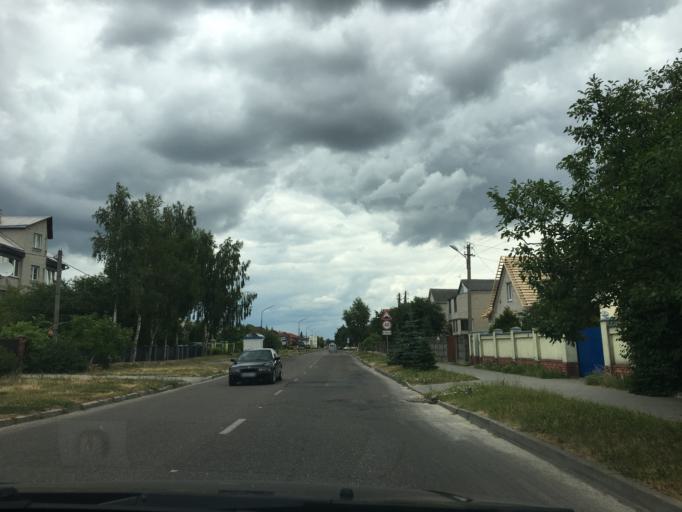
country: BY
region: Grodnenskaya
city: Hrodna
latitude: 53.6252
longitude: 23.8455
